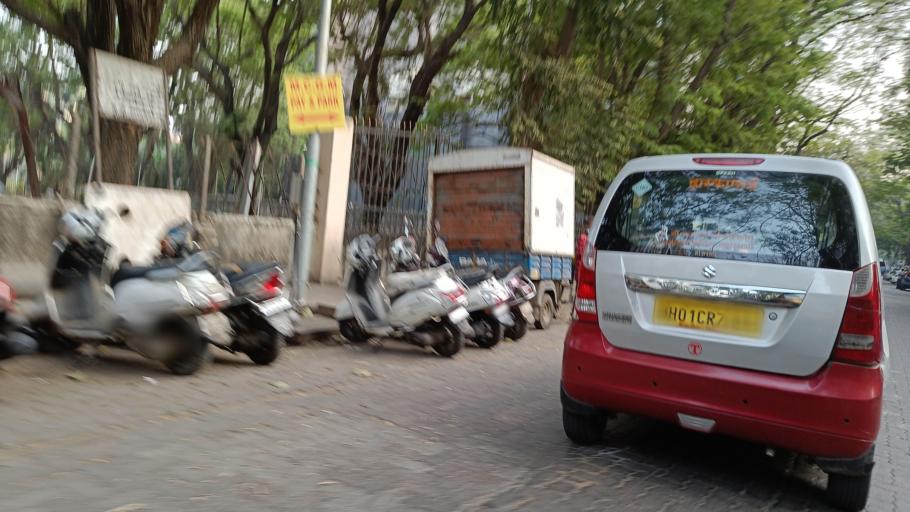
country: IN
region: Maharashtra
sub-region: Mumbai Suburban
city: Mumbai
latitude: 19.0648
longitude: 72.8332
